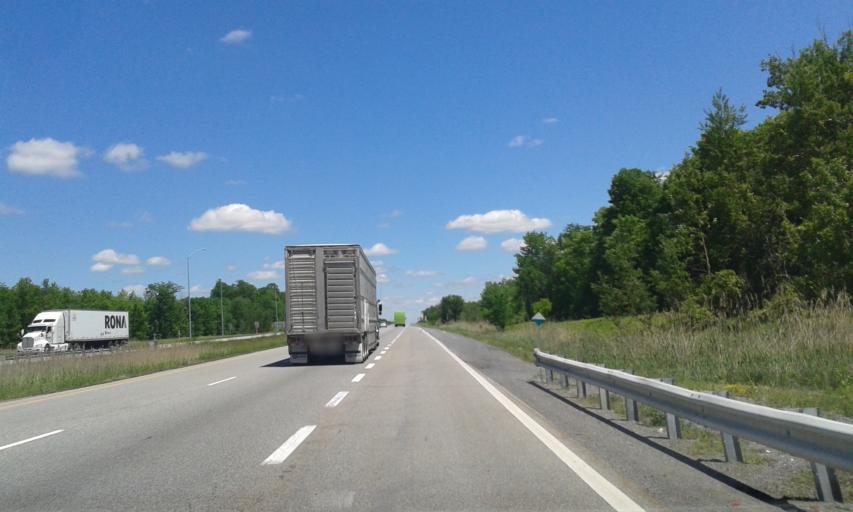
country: US
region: New York
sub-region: St. Lawrence County
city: Massena
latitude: 45.0467
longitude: -74.9067
